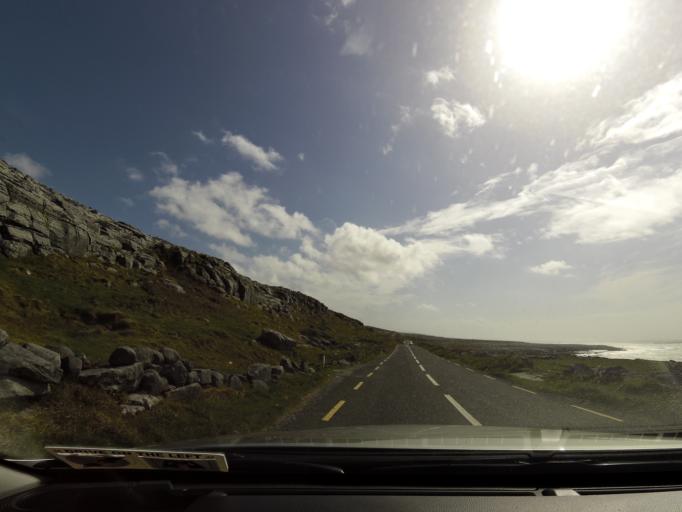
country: IE
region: Connaught
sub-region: County Galway
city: Bearna
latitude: 53.1505
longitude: -9.2689
